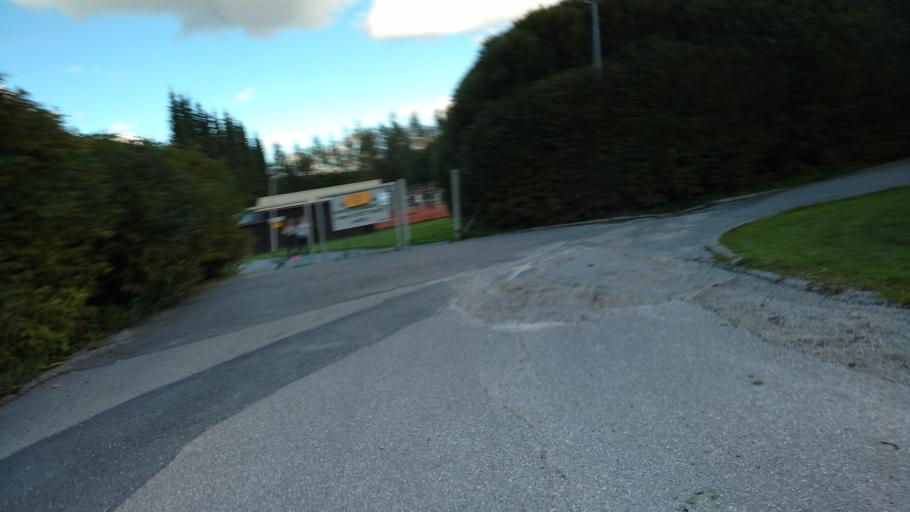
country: FI
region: Varsinais-Suomi
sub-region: Salo
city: Salo
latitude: 60.3801
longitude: 23.1404
